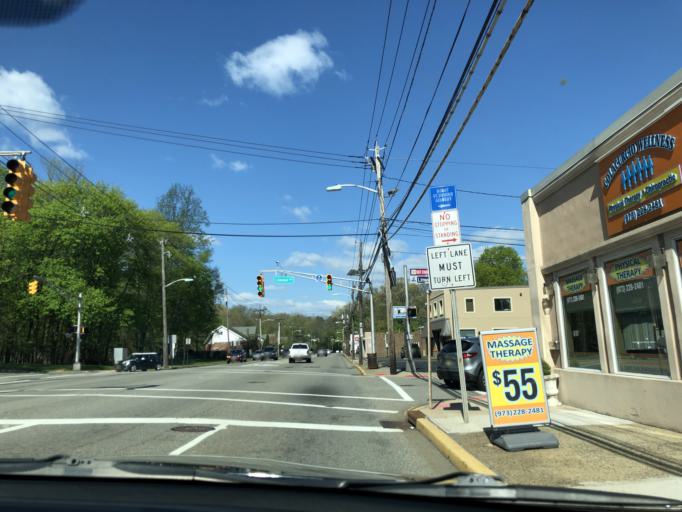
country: US
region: New Jersey
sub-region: Essex County
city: Caldwell
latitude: 40.8356
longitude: -74.2667
